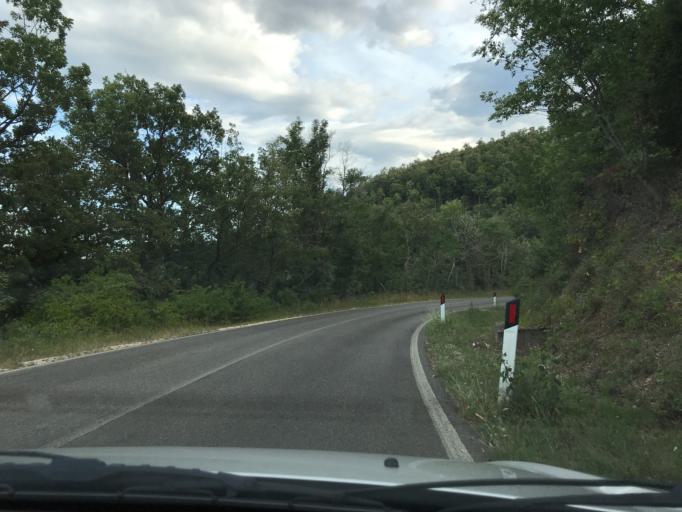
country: IT
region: Umbria
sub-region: Provincia di Terni
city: Guardea
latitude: 42.6543
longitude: 12.3507
